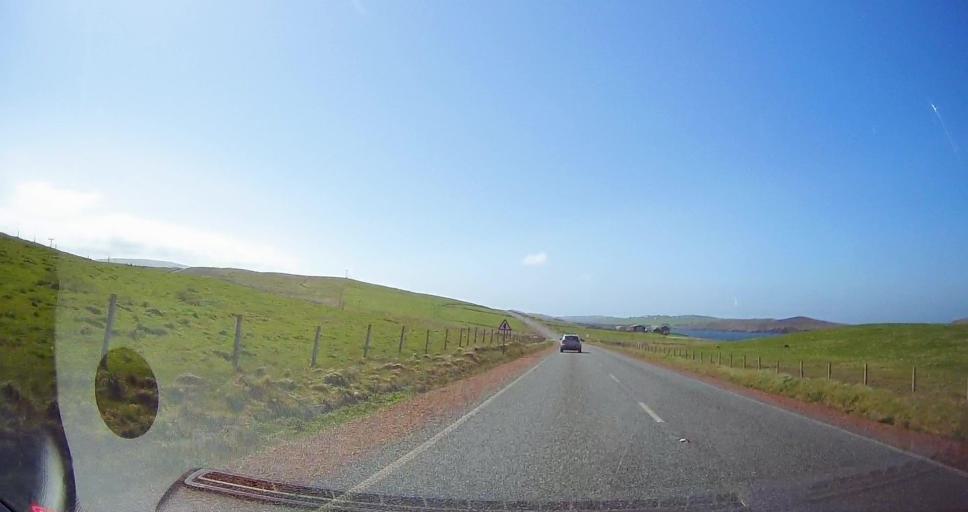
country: GB
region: Scotland
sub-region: Shetland Islands
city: Sandwick
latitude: 60.1193
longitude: -1.2899
